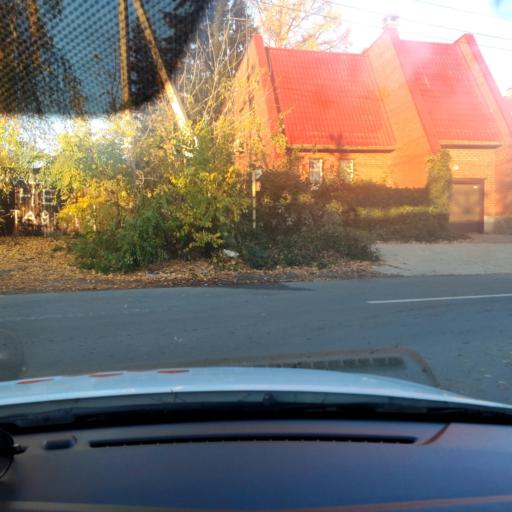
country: RU
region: Tatarstan
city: Verkhniy Uslon
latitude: 55.6217
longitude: 49.0141
